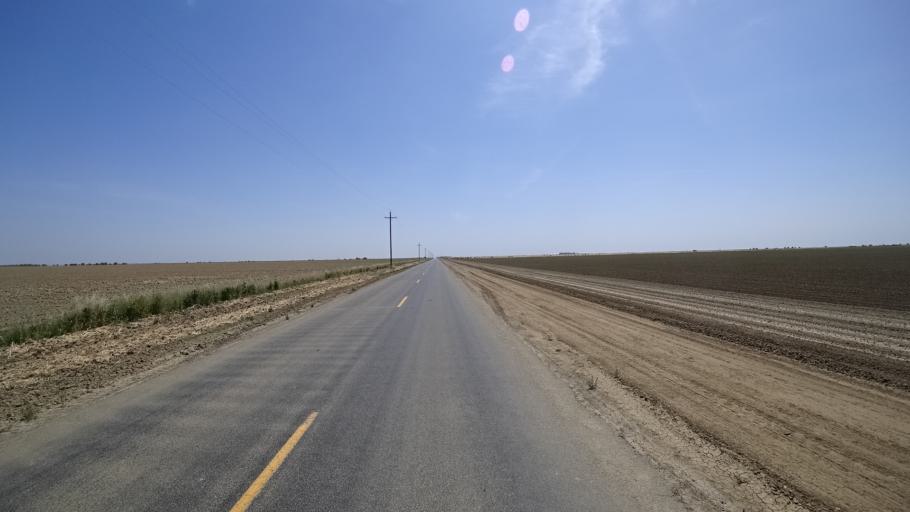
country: US
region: California
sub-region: Kings County
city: Stratford
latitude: 36.1377
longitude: -119.9367
